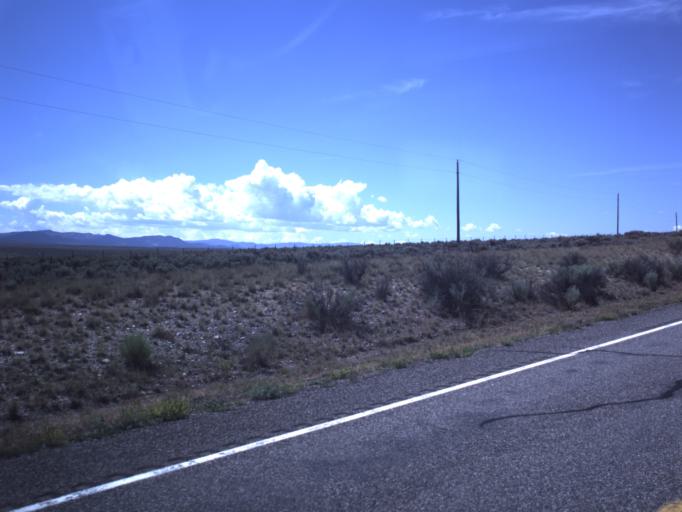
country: US
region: Utah
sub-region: Garfield County
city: Panguitch
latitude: 37.9939
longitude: -112.3902
